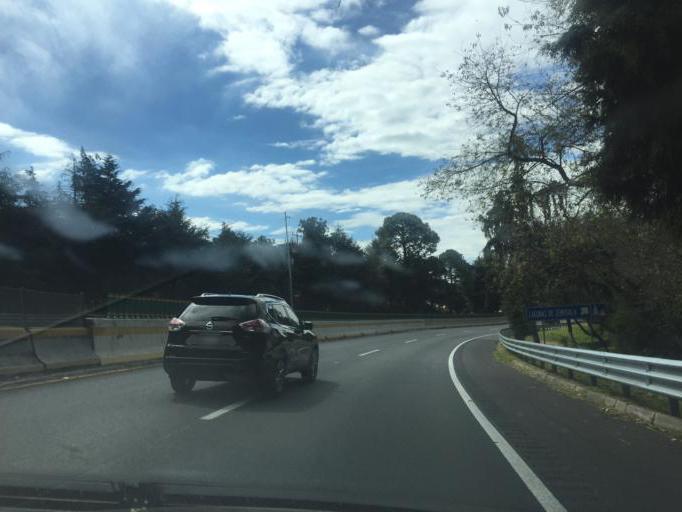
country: MX
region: Morelos
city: Tres Marias
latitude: 19.0611
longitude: -99.2387
